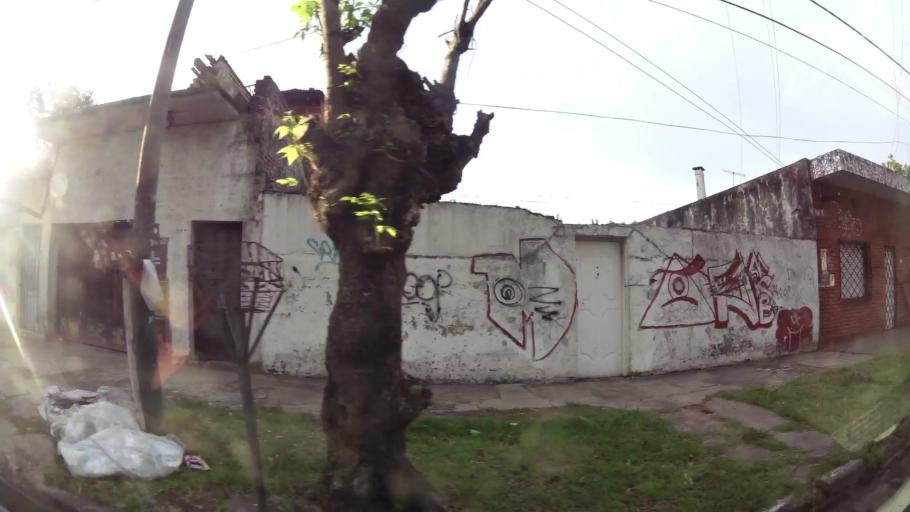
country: AR
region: Buenos Aires
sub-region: Partido de Lomas de Zamora
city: Lomas de Zamora
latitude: -34.7450
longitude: -58.3551
